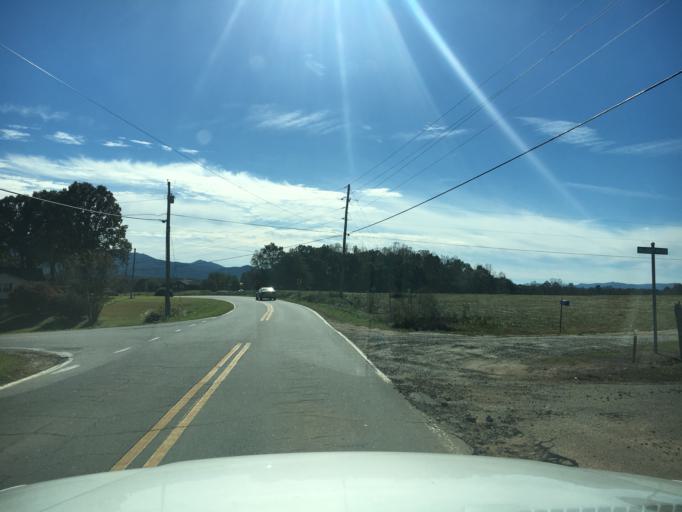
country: US
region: North Carolina
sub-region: Burke County
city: Salem
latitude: 35.7008
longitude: -81.7365
